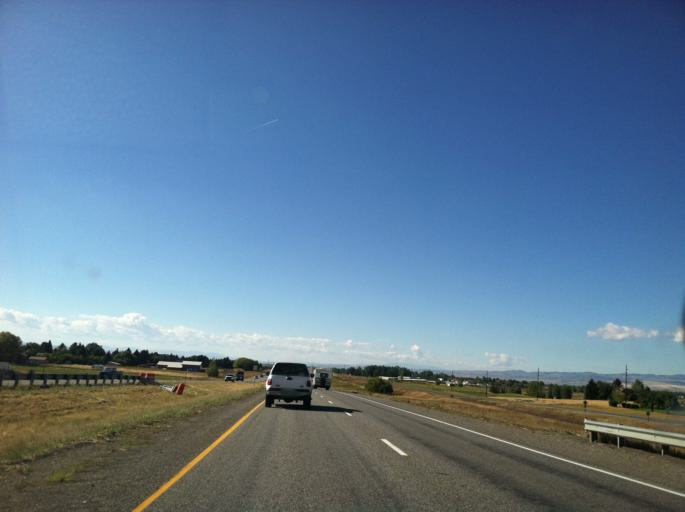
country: US
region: Montana
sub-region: Gallatin County
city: Bozeman
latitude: 45.7305
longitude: -111.0917
